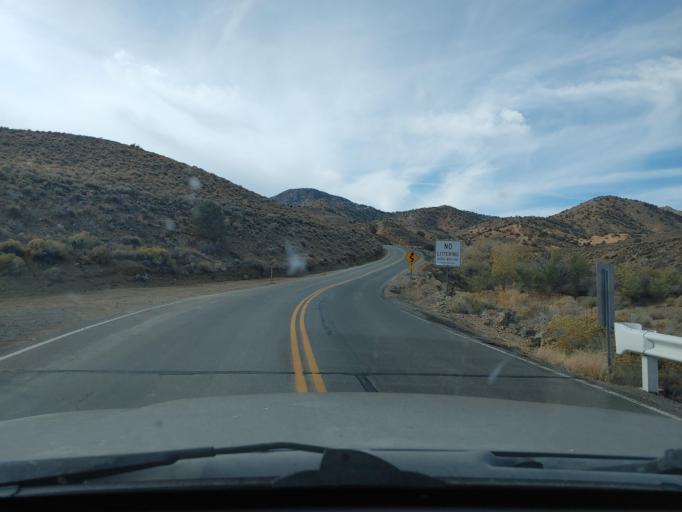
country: US
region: Nevada
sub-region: Lyon County
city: Dayton
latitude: 39.3057
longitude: -119.5632
